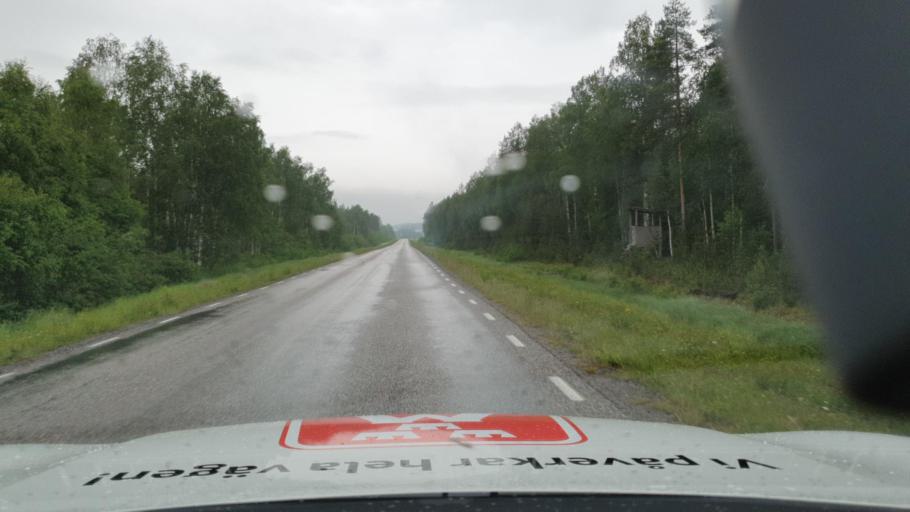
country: SE
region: Vaesterbotten
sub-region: Vannas Kommun
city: Vaennaes
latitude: 63.7828
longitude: 19.5877
